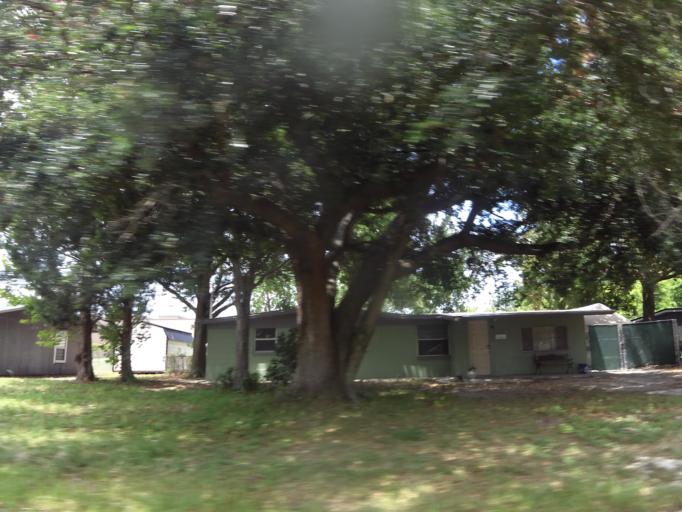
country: US
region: Florida
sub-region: Duval County
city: Atlantic Beach
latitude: 30.3305
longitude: -81.4156
